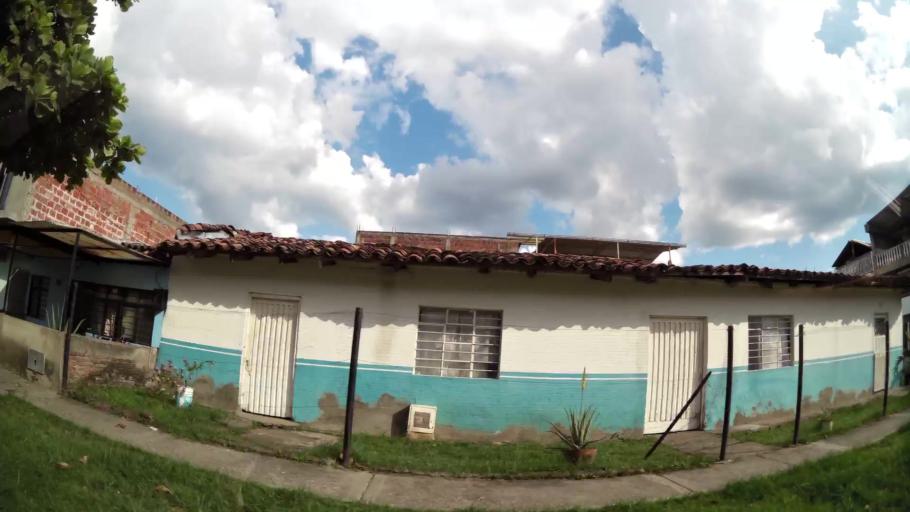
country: CO
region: Valle del Cauca
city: Cali
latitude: 3.4070
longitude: -76.5122
